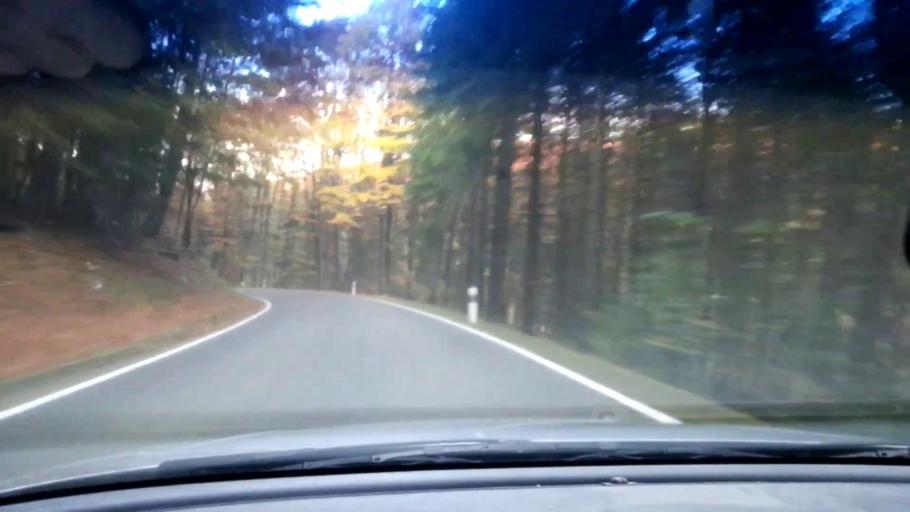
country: DE
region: Bavaria
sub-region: Upper Franconia
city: Heiligenstadt
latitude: 49.8611
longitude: 11.1249
